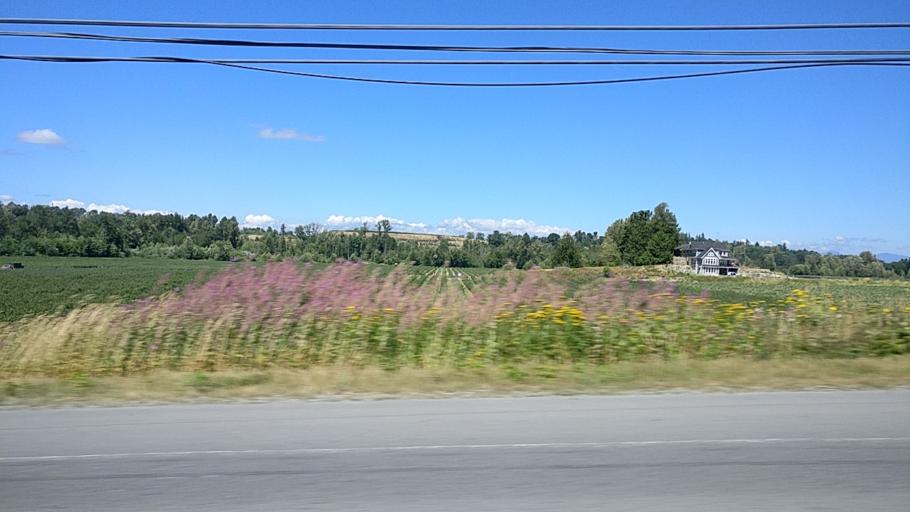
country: CA
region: British Columbia
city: Aldergrove
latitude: 49.0168
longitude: -122.4341
